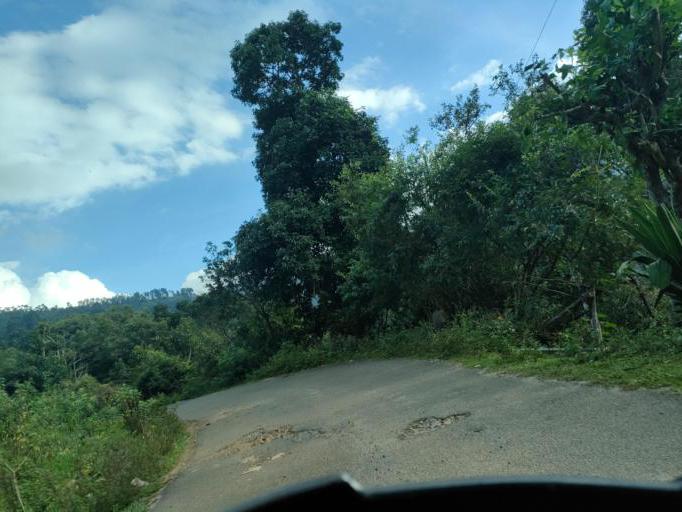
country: IN
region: Tamil Nadu
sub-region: Dindigul
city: Kodaikanal
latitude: 10.2790
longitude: 77.5305
